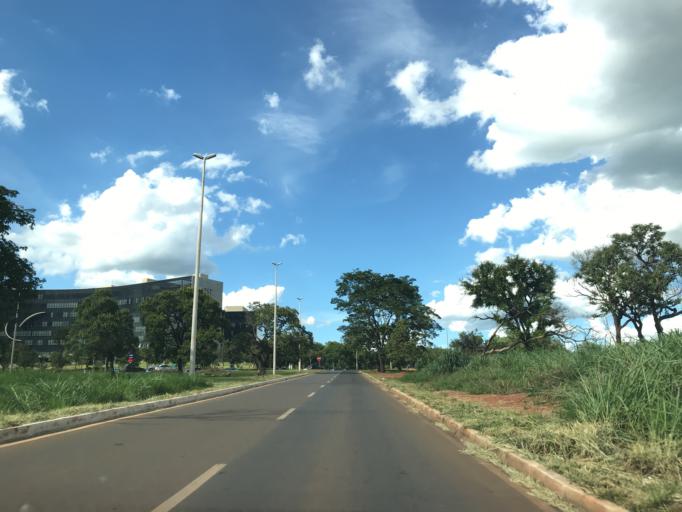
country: BR
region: Federal District
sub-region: Brasilia
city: Brasilia
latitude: -15.8148
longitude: -47.8678
